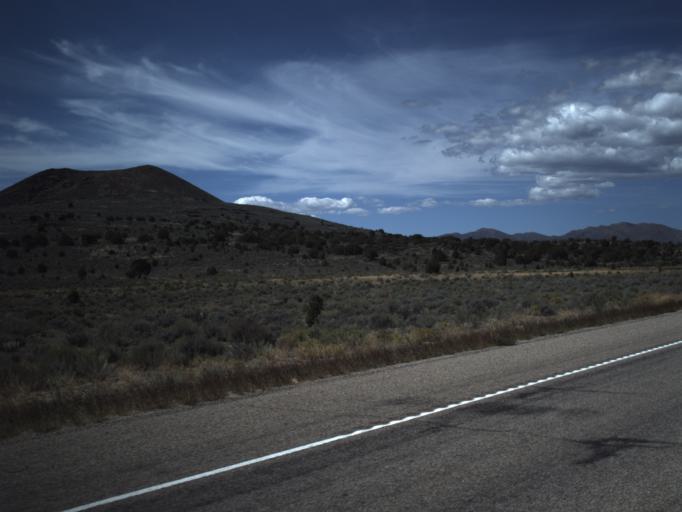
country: US
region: Utah
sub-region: Washington County
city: Ivins
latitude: 37.3134
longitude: -113.6762
